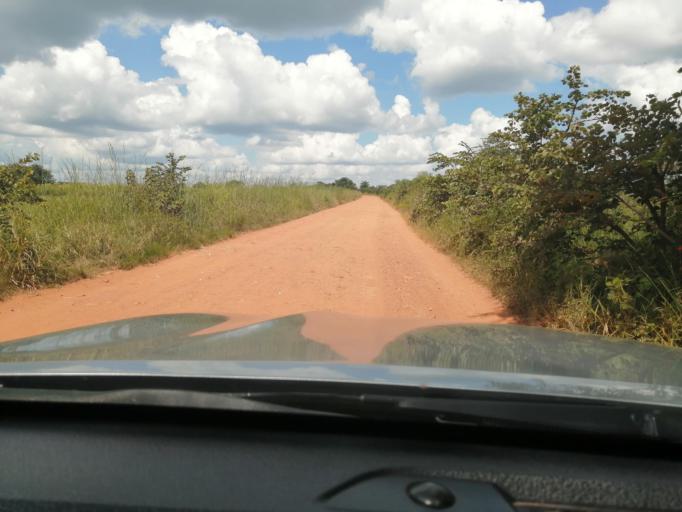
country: ZM
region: Lusaka
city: Lusaka
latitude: -15.1949
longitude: 27.9894
